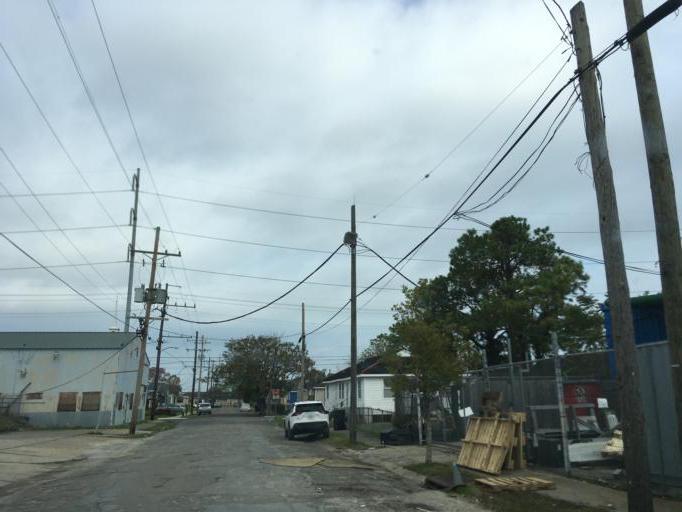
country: US
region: Louisiana
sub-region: Orleans Parish
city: New Orleans
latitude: 29.9880
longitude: -90.0597
